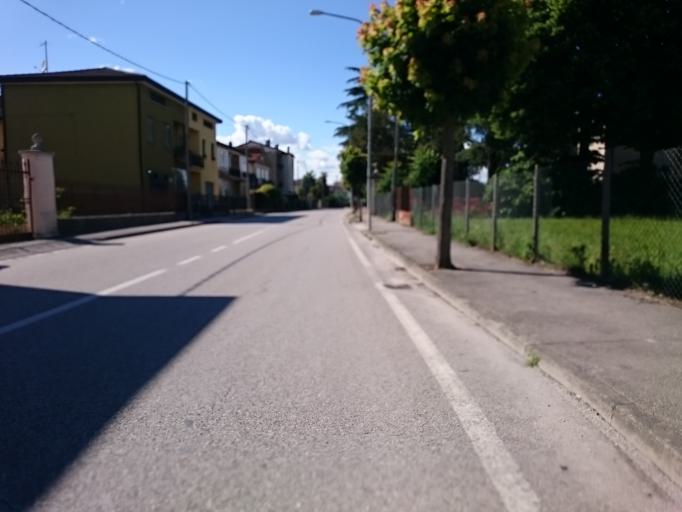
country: IT
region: Veneto
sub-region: Provincia di Padova
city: Saonara
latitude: 45.3656
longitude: 11.9872
